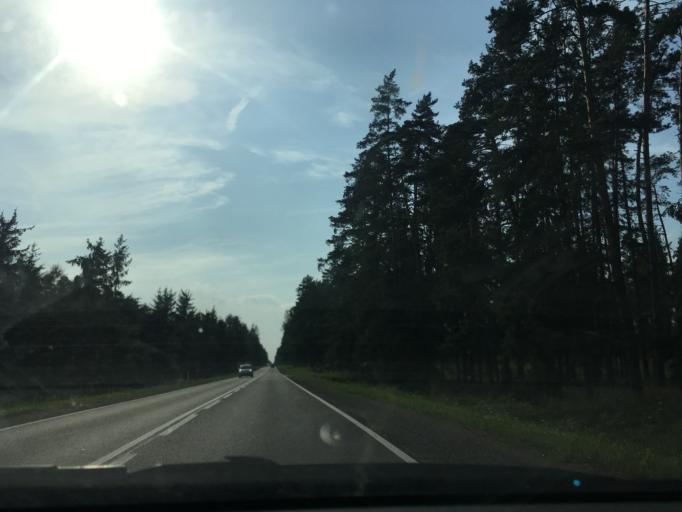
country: PL
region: Podlasie
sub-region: Powiat bialostocki
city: Suprasl
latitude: 53.1256
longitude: 23.3630
